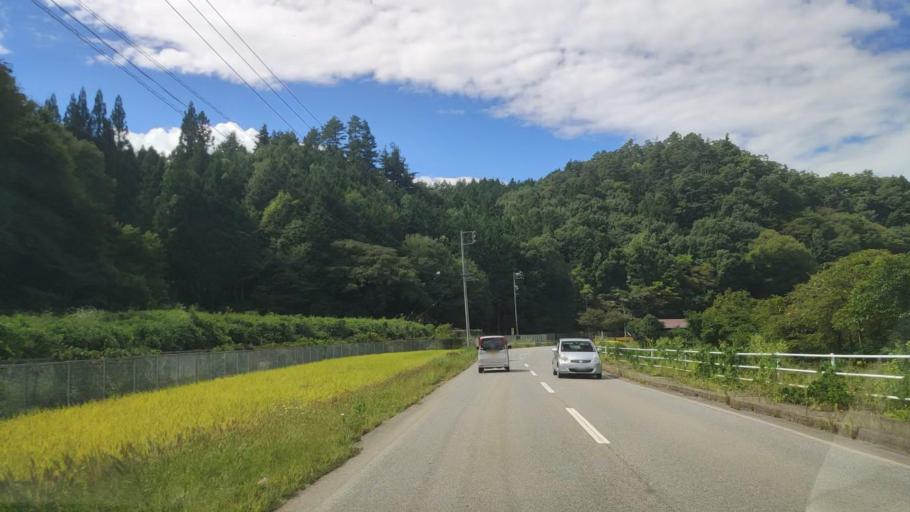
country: JP
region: Gifu
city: Takayama
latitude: 36.1782
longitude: 137.2636
